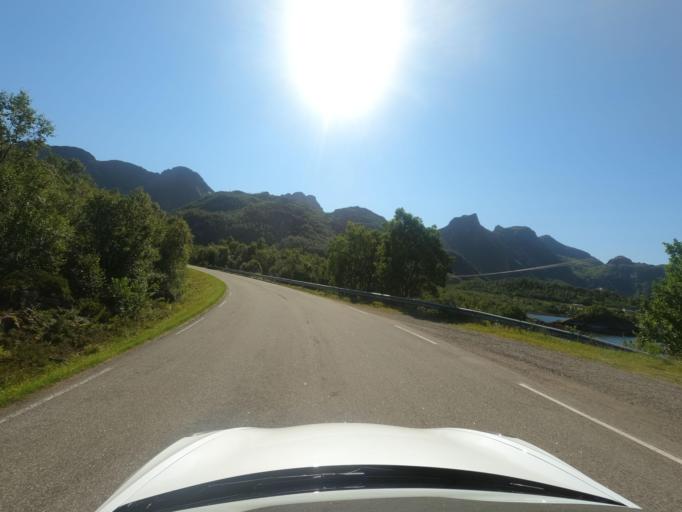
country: NO
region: Nordland
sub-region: Hadsel
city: Stokmarknes
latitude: 68.3572
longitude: 15.0628
